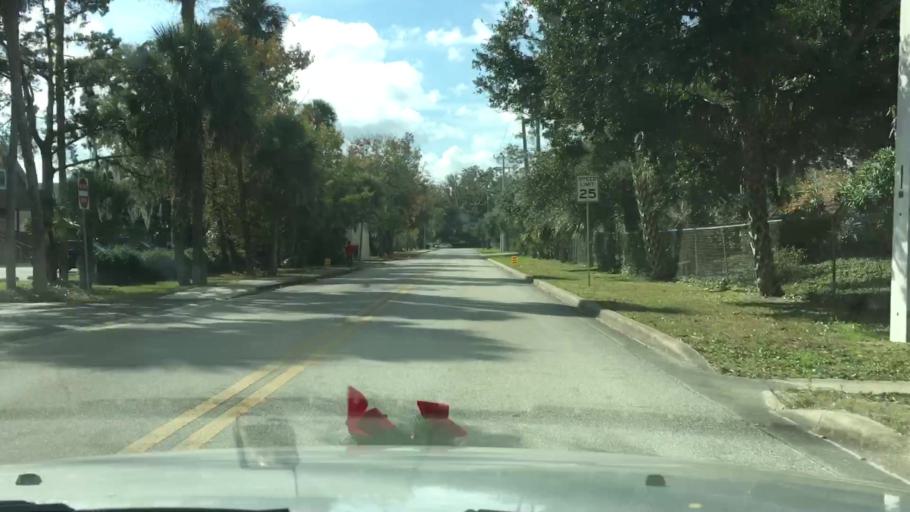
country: US
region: Florida
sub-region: Volusia County
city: Ormond Beach
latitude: 29.2833
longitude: -81.0676
